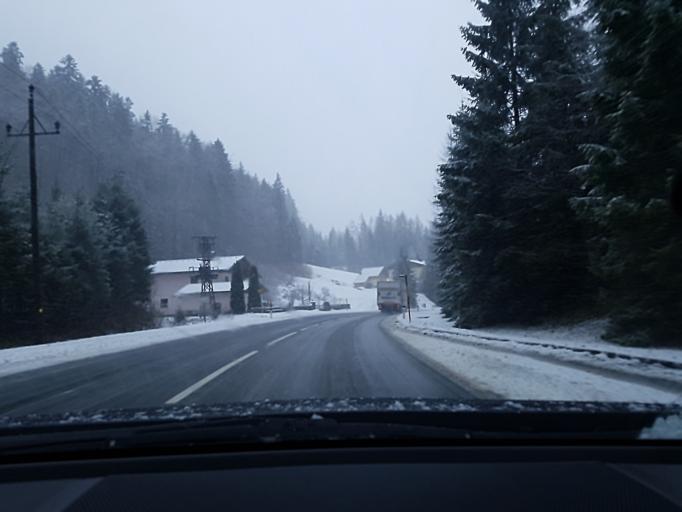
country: AT
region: Salzburg
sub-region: Politischer Bezirk Hallein
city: Scheffau am Tennengebirge
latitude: 47.5847
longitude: 13.2699
